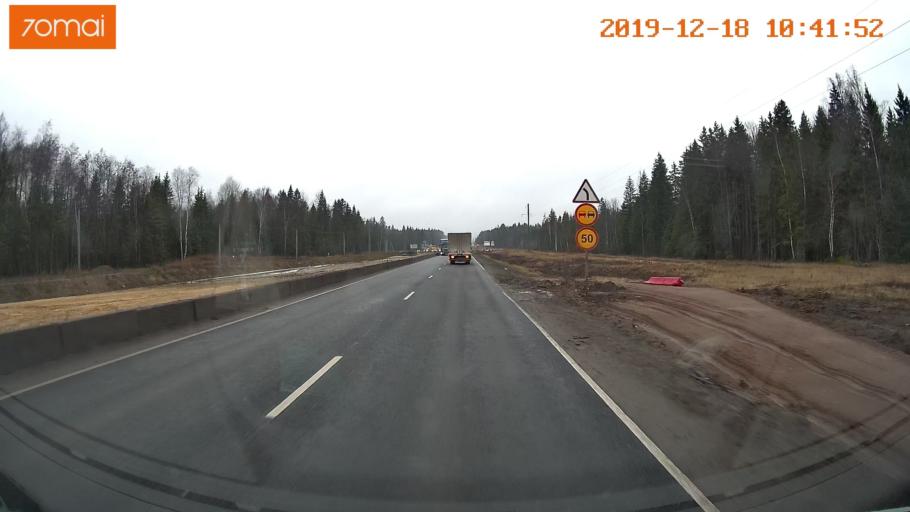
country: RU
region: Moskovskaya
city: Aprelevka
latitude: 55.4592
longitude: 37.1039
